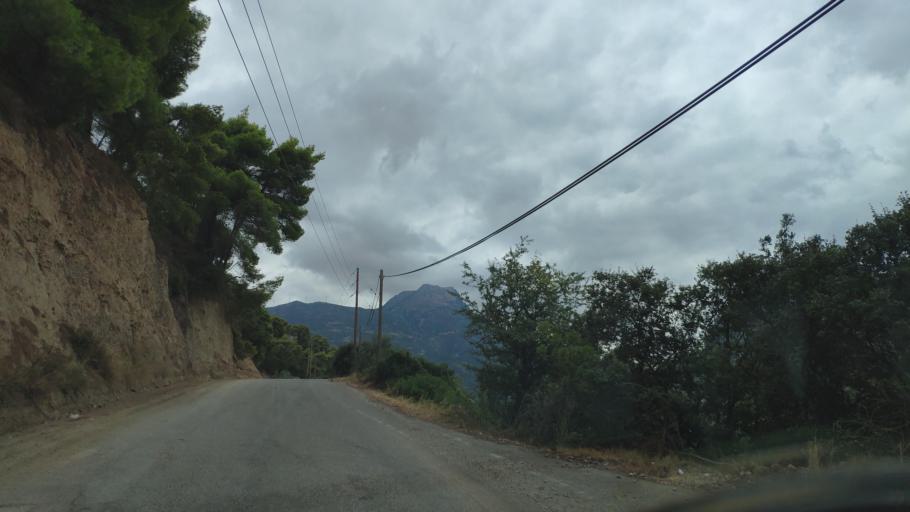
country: GR
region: West Greece
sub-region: Nomos Achaias
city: Temeni
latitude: 38.1895
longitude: 22.1507
